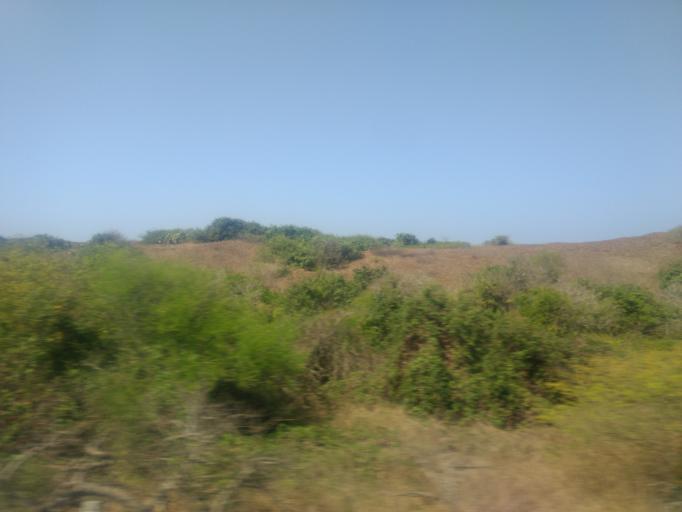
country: MX
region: Colima
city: Armeria
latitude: 18.9527
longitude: -104.1307
